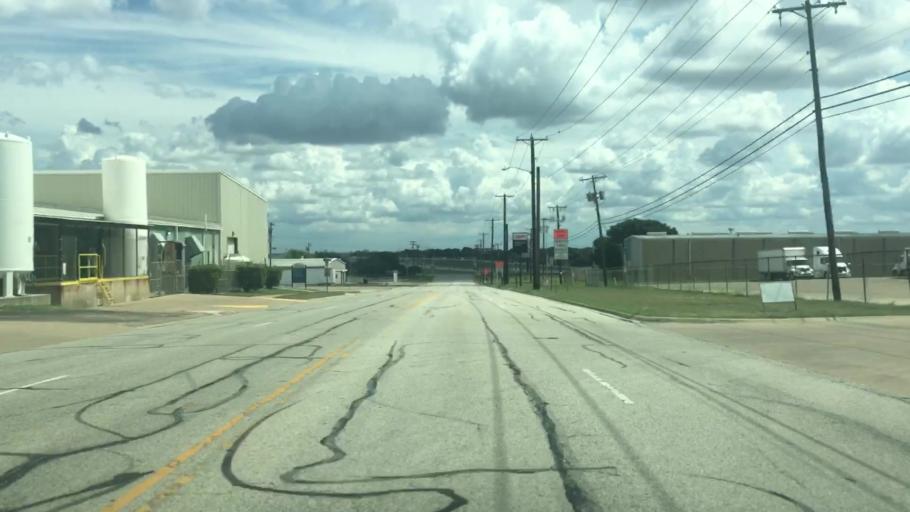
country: US
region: Texas
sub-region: Bell County
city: Temple
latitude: 31.1276
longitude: -97.3456
